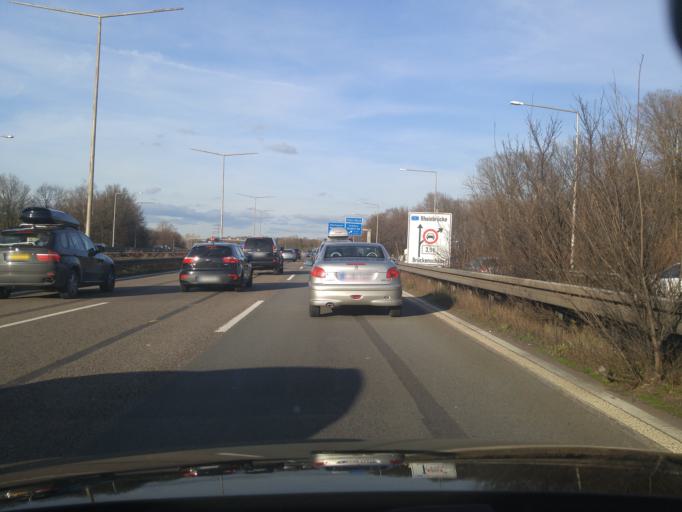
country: DE
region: North Rhine-Westphalia
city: Opladen
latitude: 51.0410
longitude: 7.0079
